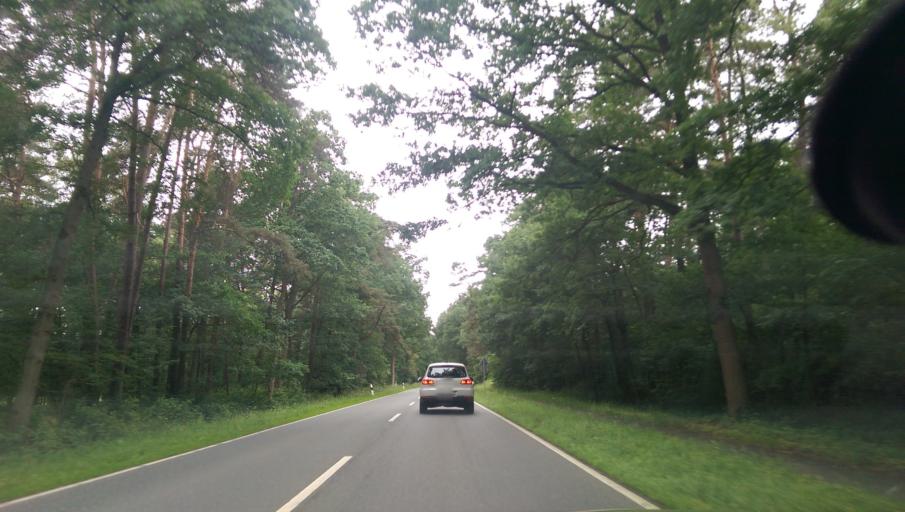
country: DE
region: Lower Saxony
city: Rotenburg
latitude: 53.0767
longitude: 9.4319
